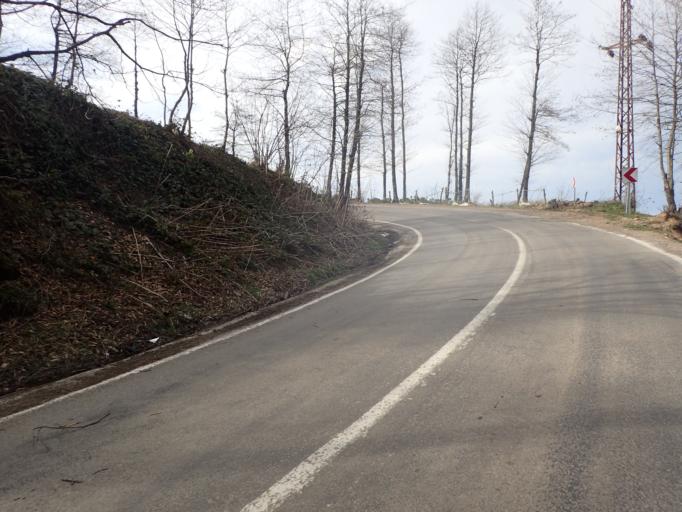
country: TR
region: Ordu
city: Camas
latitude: 40.8911
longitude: 37.5259
